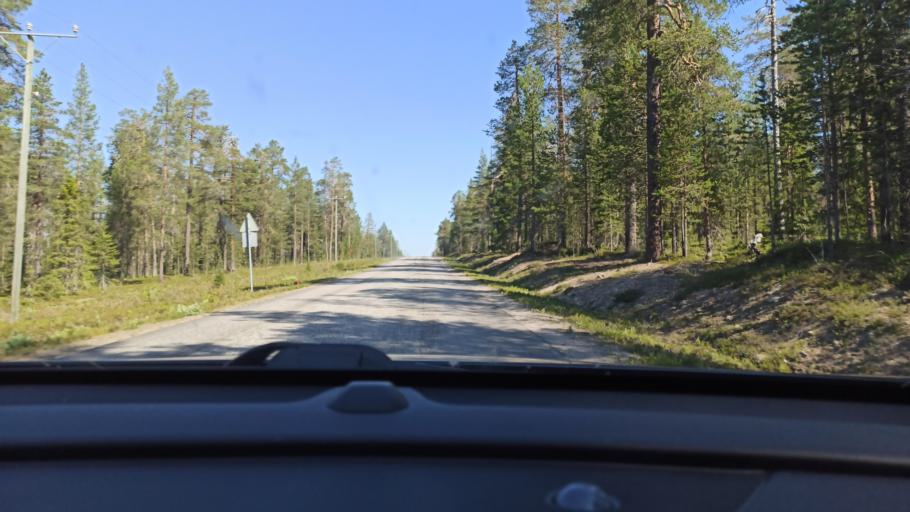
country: FI
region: Lapland
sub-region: Tunturi-Lappi
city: Kolari
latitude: 67.6389
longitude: 24.1570
